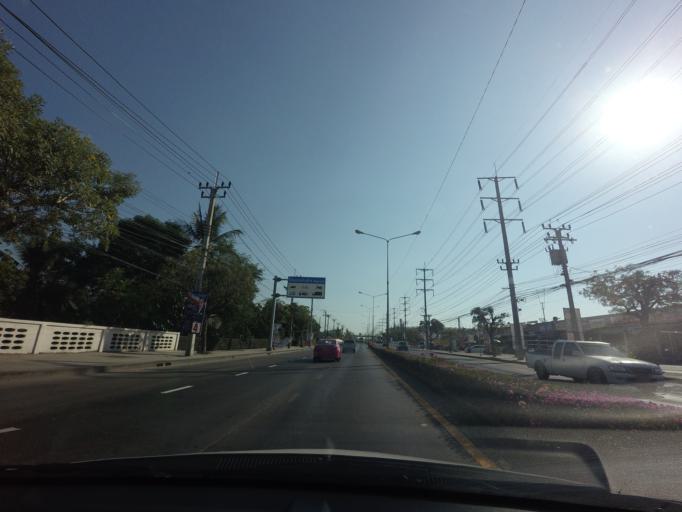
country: TH
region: Bangkok
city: Nong Chok
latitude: 13.8372
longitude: 100.8534
